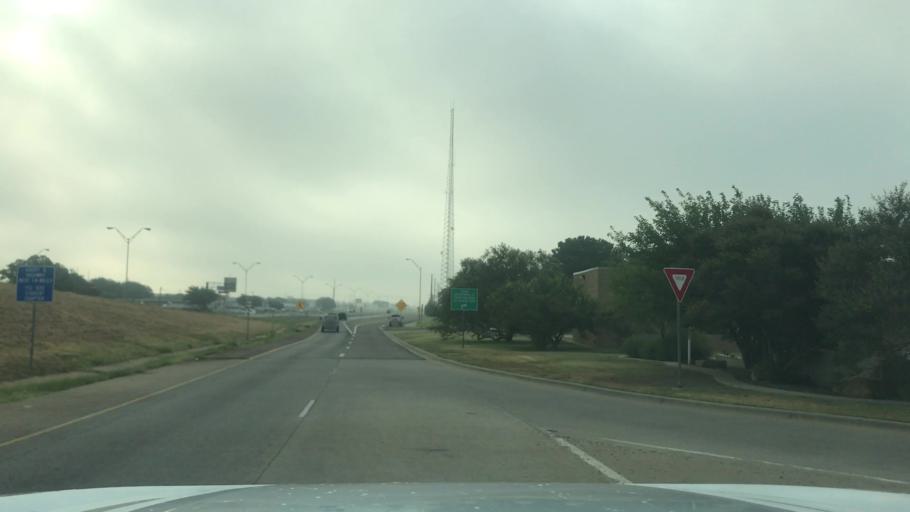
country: US
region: Texas
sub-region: Lubbock County
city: Lubbock
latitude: 33.5366
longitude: -101.8434
